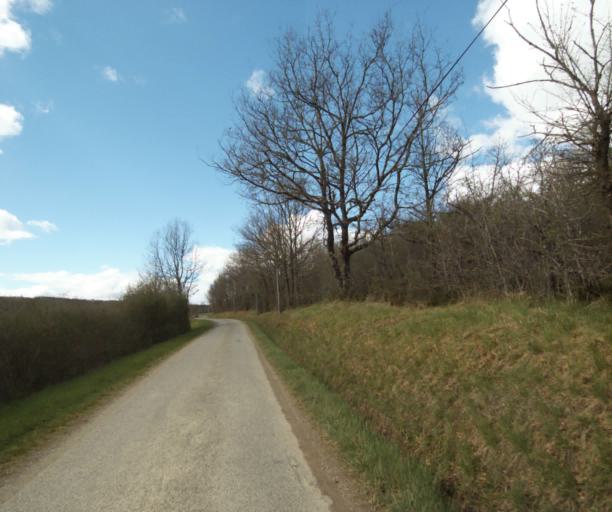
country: FR
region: Midi-Pyrenees
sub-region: Departement de l'Ariege
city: Saverdun
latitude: 43.1907
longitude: 1.5632
